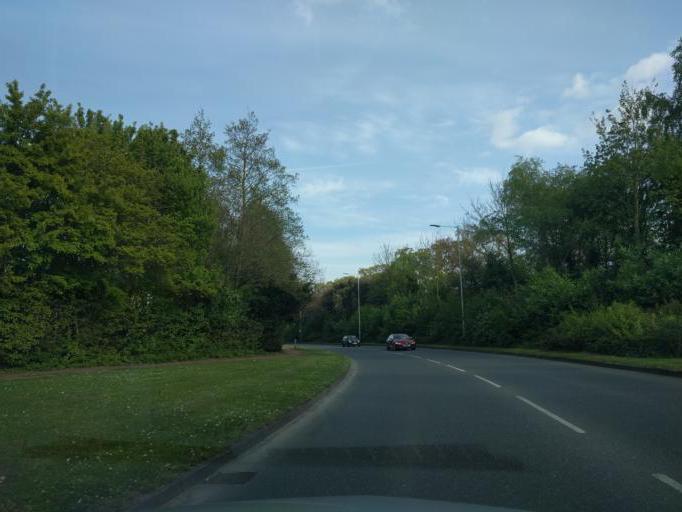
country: GB
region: England
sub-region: Suffolk
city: Bury St Edmunds
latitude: 52.2436
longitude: 0.7450
